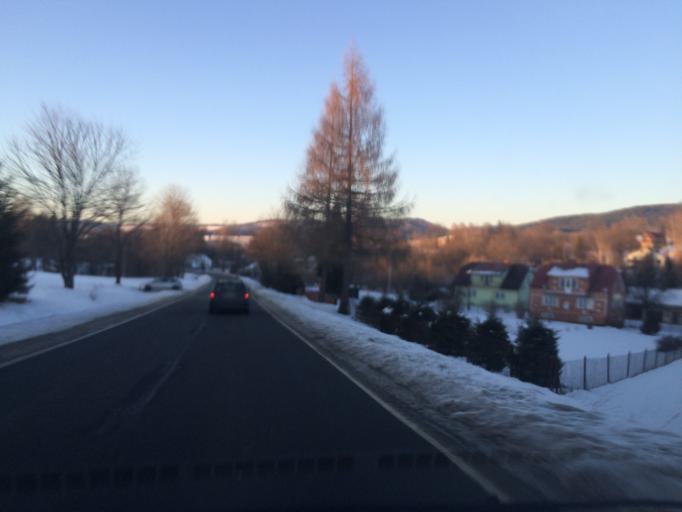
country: PL
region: Subcarpathian Voivodeship
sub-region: Powiat bieszczadzki
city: Czarna
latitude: 49.3180
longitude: 22.6725
